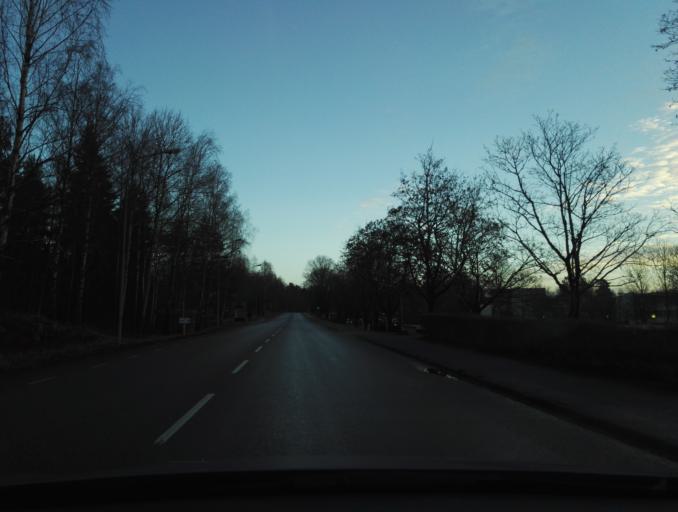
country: SE
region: Kronoberg
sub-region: Vaxjo Kommun
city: Vaexjoe
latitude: 56.8989
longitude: 14.7891
